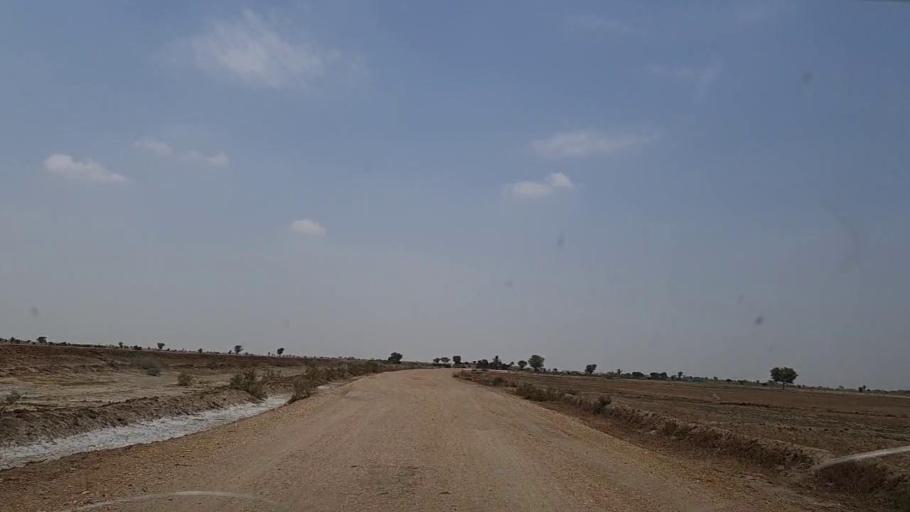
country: PK
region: Sindh
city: Phulji
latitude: 26.8012
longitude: 67.6354
